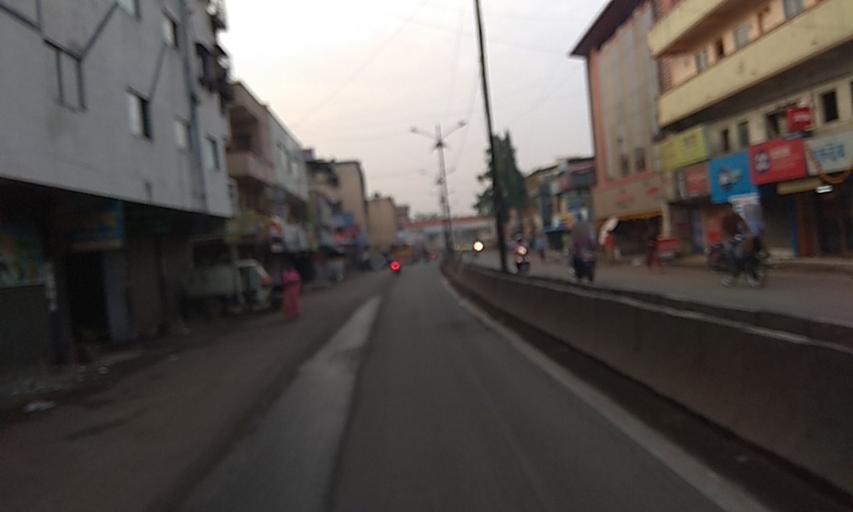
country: IN
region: Maharashtra
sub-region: Pune Division
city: Lohogaon
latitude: 18.5613
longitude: 73.9280
